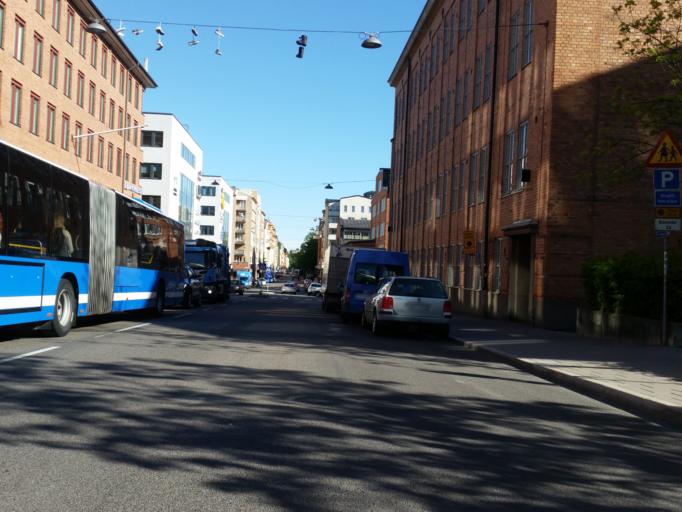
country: SE
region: Stockholm
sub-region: Stockholms Kommun
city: Arsta
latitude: 59.3109
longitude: 18.0586
